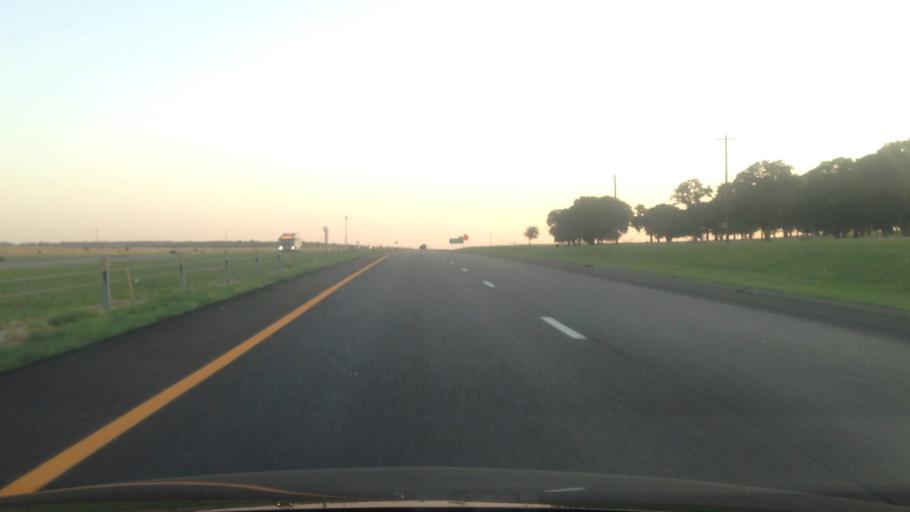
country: US
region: Texas
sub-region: Denton County
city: Argyle
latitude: 33.1501
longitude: -97.1944
